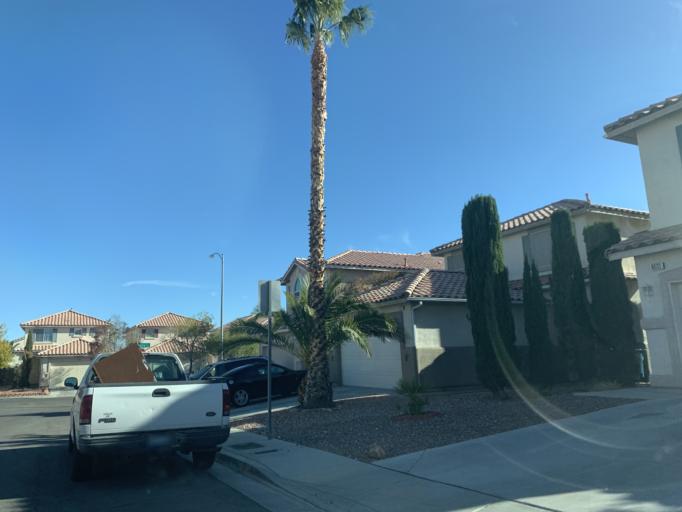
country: US
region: Nevada
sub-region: Clark County
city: Summerlin South
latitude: 36.1213
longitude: -115.3003
